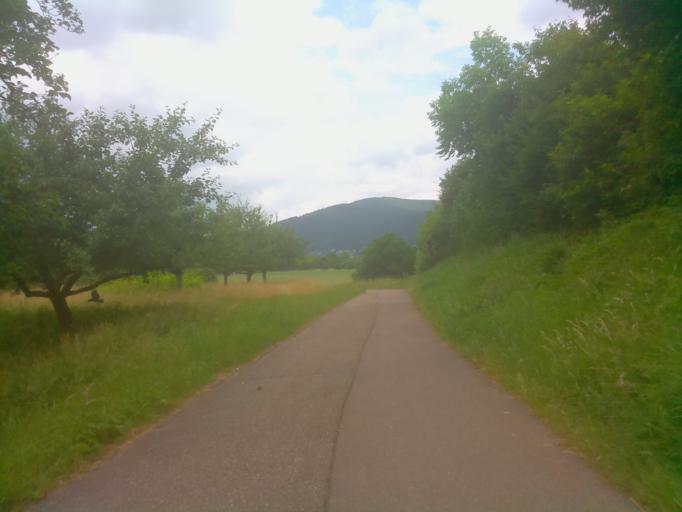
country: DE
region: Baden-Wuerttemberg
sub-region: Karlsruhe Region
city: Eberbach
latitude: 49.4604
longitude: 8.9660
